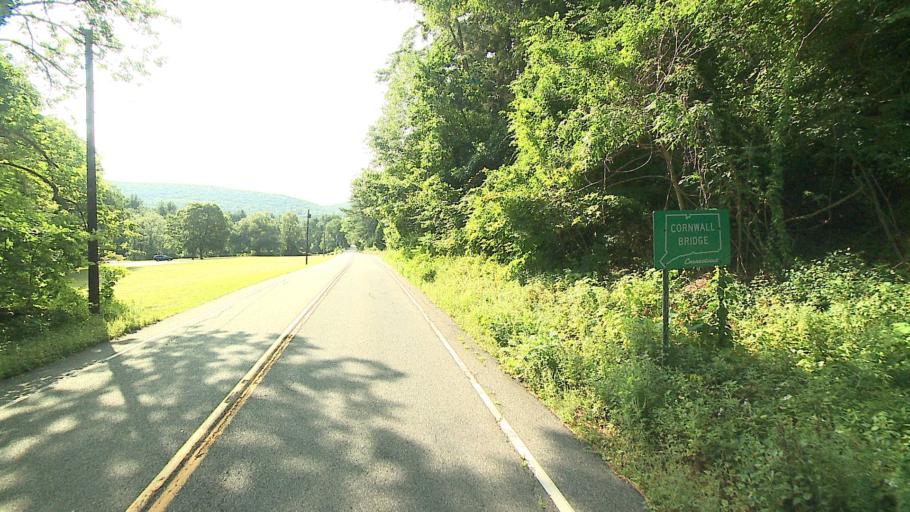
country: US
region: Connecticut
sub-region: Litchfield County
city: Kent
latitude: 41.8254
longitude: -73.3795
